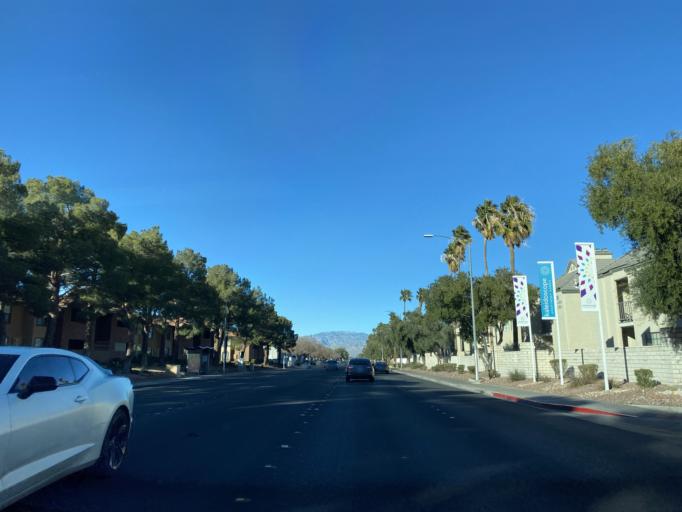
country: US
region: Nevada
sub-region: Clark County
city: Spring Valley
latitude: 36.2059
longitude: -115.2423
